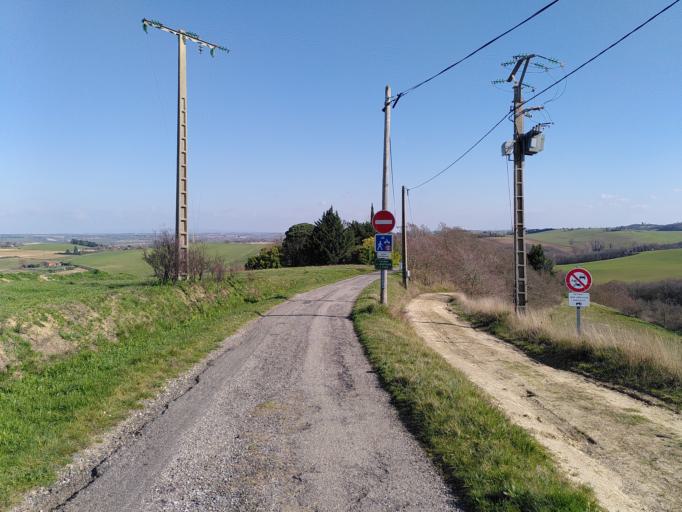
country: FR
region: Midi-Pyrenees
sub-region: Departement de la Haute-Garonne
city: Pompertuzat
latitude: 43.4663
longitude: 1.5231
